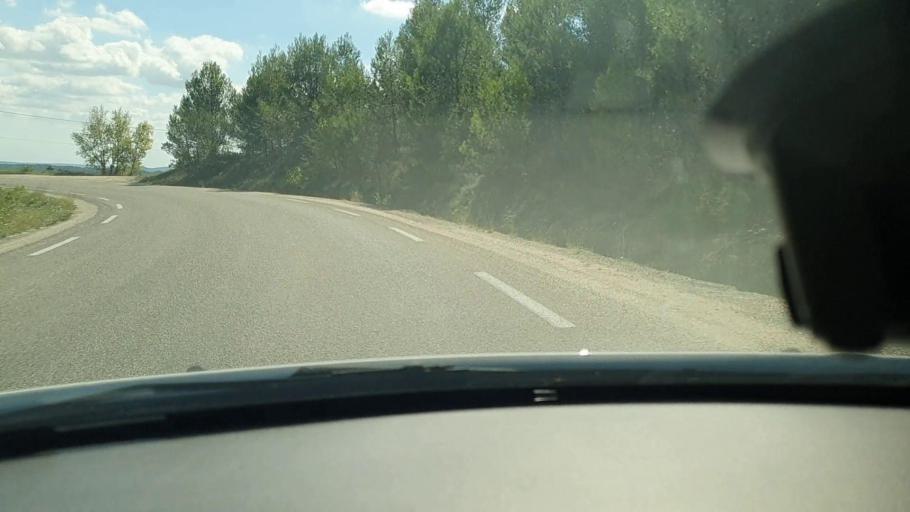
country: FR
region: Languedoc-Roussillon
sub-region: Departement du Gard
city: Sabran
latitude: 44.1512
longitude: 4.4840
